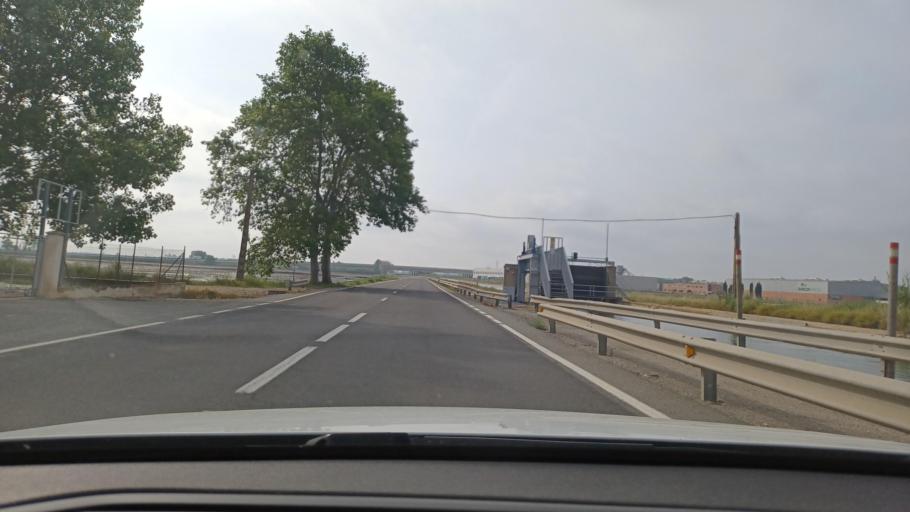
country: ES
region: Catalonia
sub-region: Provincia de Tarragona
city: Amposta
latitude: 40.7177
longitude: 0.5878
